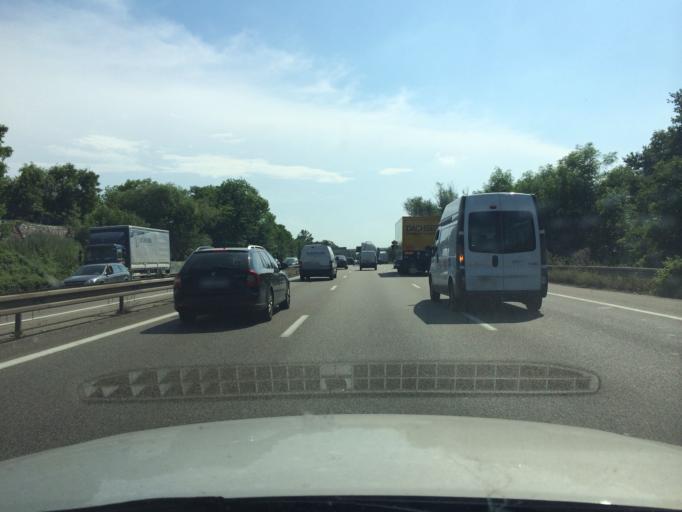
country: FR
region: Alsace
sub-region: Departement du Bas-Rhin
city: Ostwald
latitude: 48.5432
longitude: 7.7238
